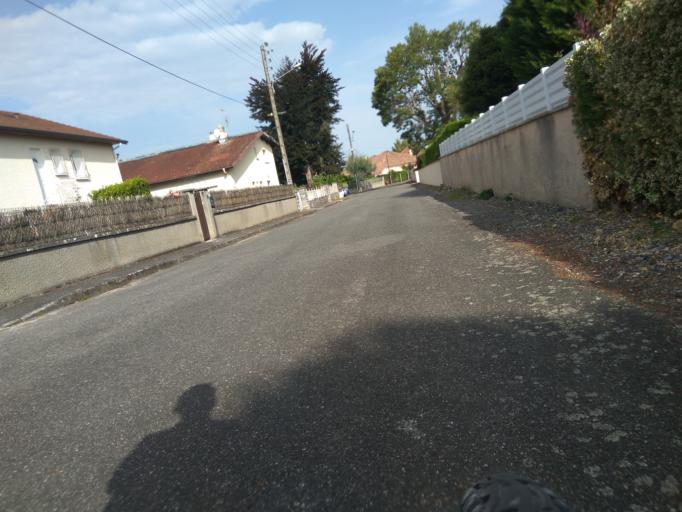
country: FR
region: Aquitaine
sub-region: Departement des Pyrenees-Atlantiques
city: Mazeres-Lezons
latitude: 43.2712
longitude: -0.3425
